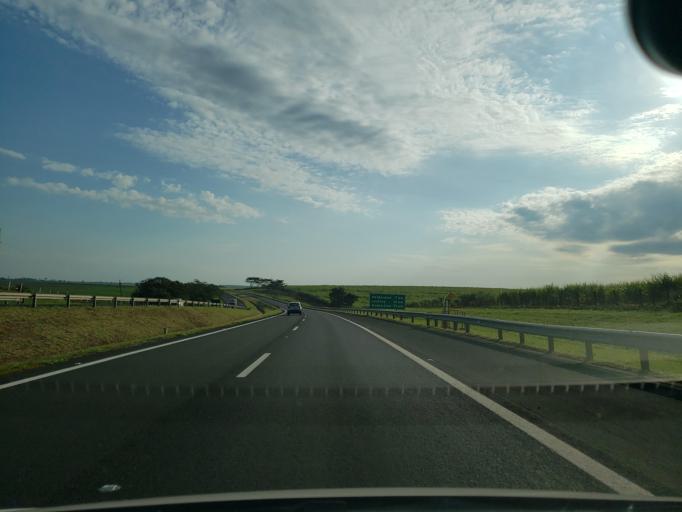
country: BR
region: Sao Paulo
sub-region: Valparaiso
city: Valparaiso
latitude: -21.2043
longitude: -50.8051
